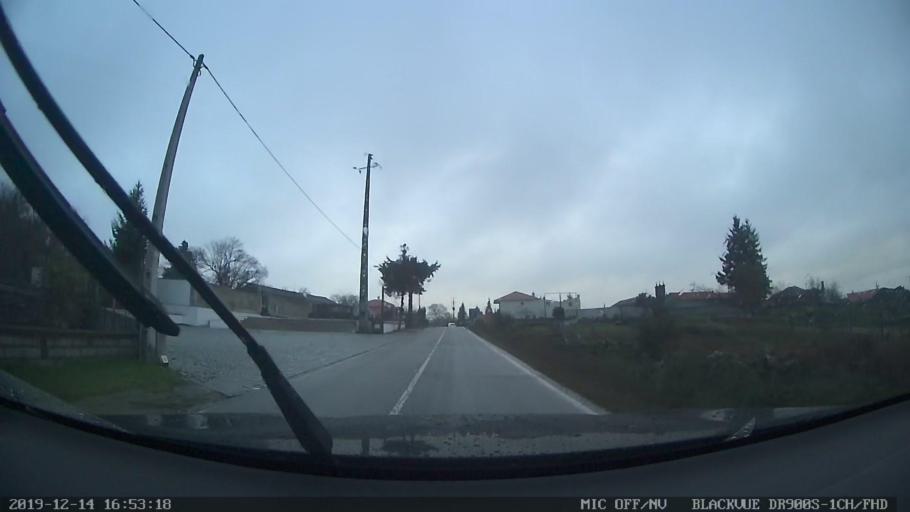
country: PT
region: Vila Real
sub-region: Murca
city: Murca
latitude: 41.4298
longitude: -7.5166
